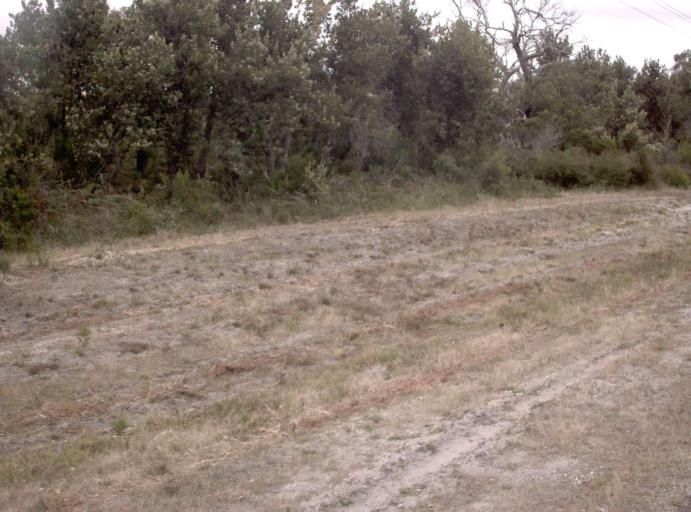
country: AU
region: Victoria
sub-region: East Gippsland
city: Bairnsdale
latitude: -38.0641
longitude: 147.5587
